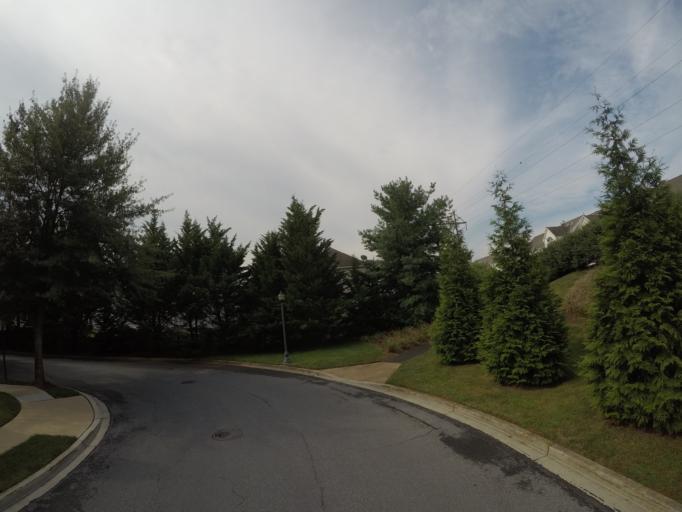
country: US
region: Maryland
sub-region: Frederick County
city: Clover Hill
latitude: 39.4558
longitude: -77.3897
